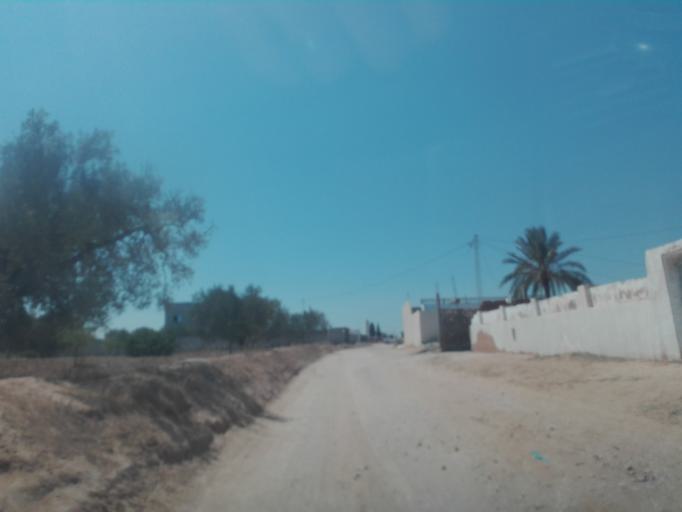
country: TN
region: Safaqis
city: Jabinyanah
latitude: 35.1079
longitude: 10.9063
